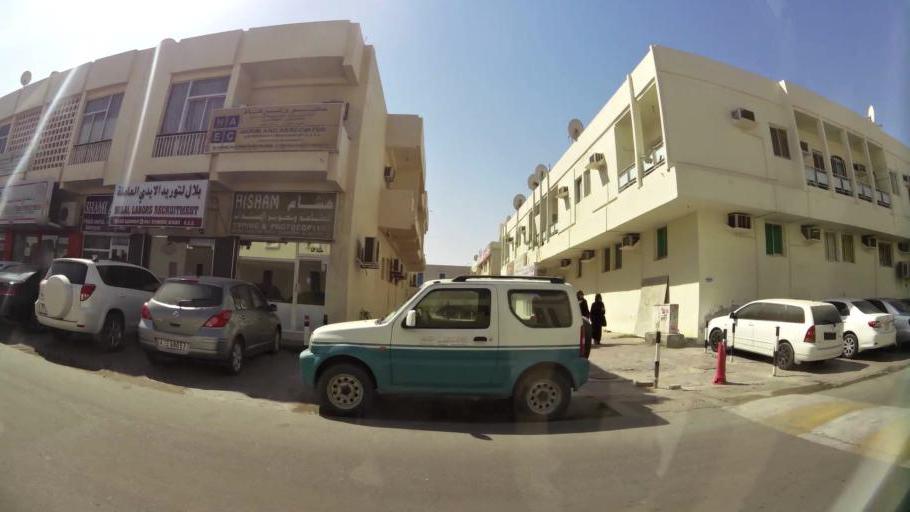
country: AE
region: Ajman
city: Ajman
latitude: 25.4072
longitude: 55.4456
